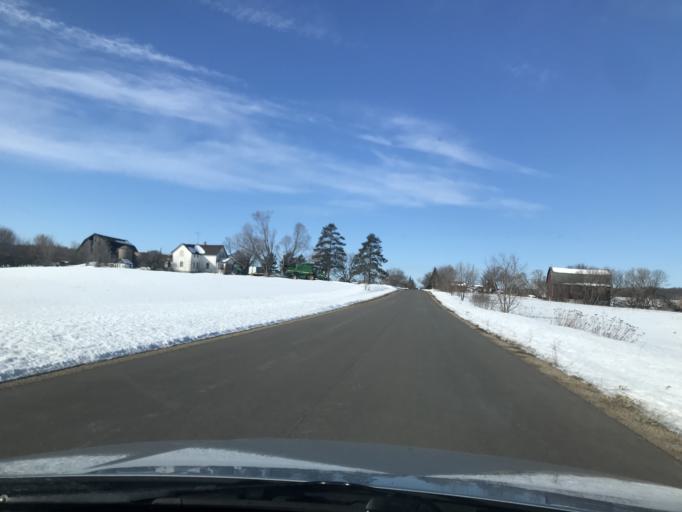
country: US
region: Wisconsin
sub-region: Oconto County
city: Gillett
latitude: 44.9396
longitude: -88.2558
